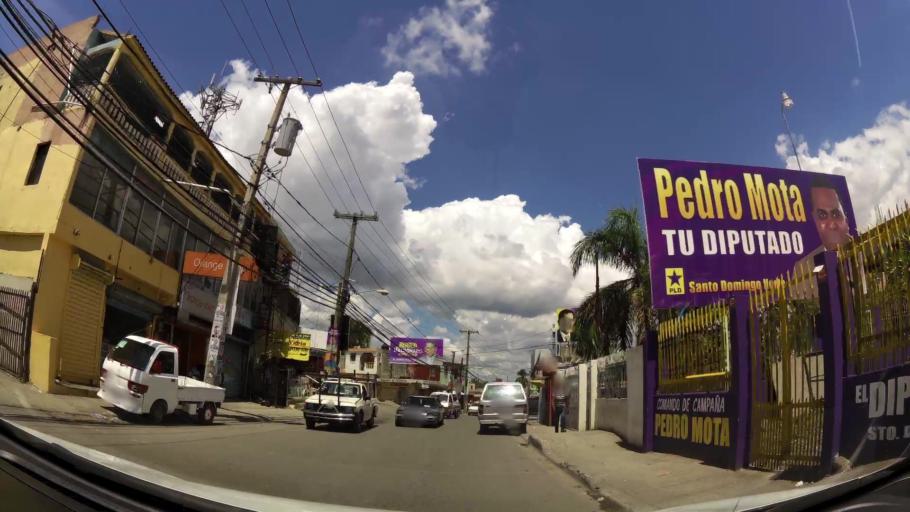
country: DO
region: Santo Domingo
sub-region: Santo Domingo
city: Santo Domingo Este
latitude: 18.5351
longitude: -69.8655
